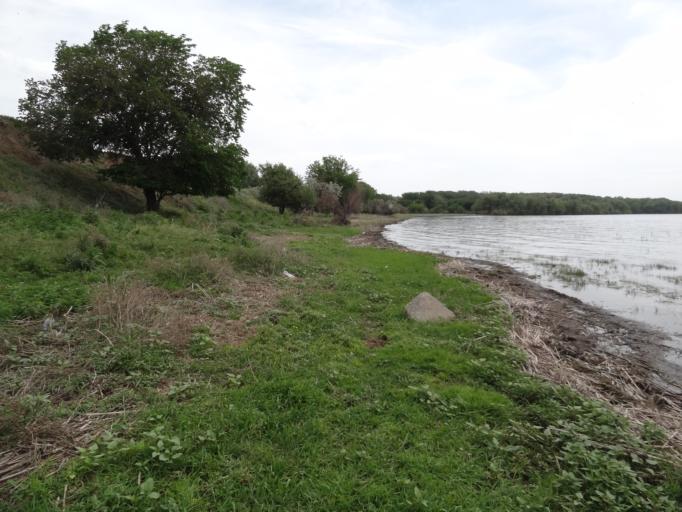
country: RU
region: Saratov
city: Privolzhskiy
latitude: 51.1972
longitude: 45.9088
